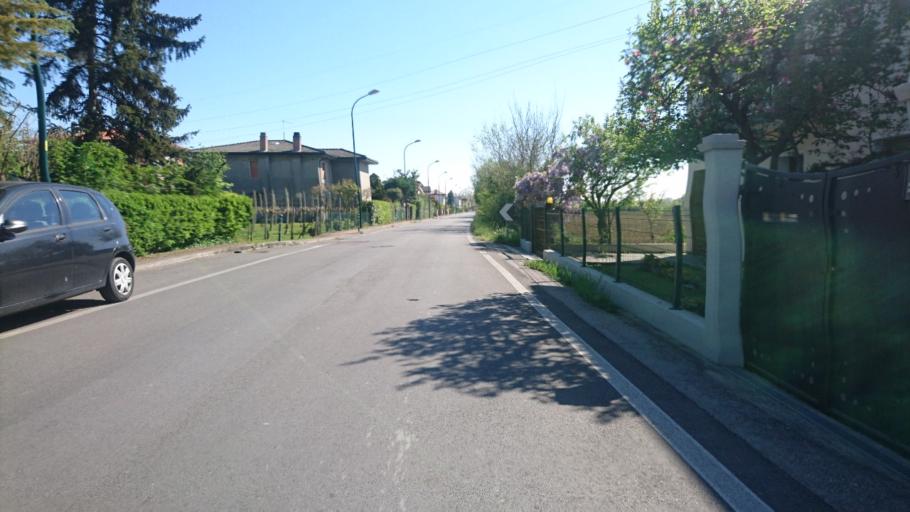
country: IT
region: Veneto
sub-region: Provincia di Venezia
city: Dese
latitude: 45.5271
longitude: 12.2687
